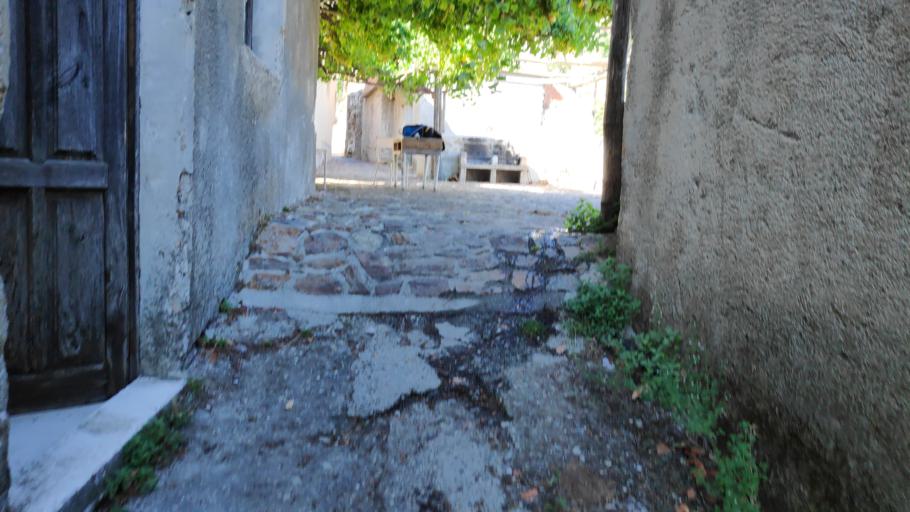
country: IT
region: Calabria
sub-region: Provincia di Reggio Calabria
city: Roccaforte del Greco
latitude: 38.0491
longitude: 15.9169
